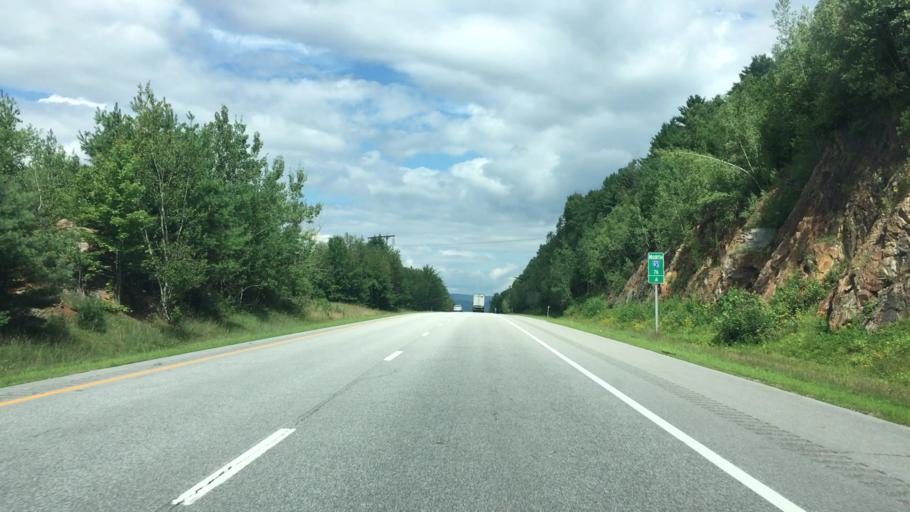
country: US
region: New Hampshire
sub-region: Grafton County
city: Ashland
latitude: 43.7157
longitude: -71.6517
